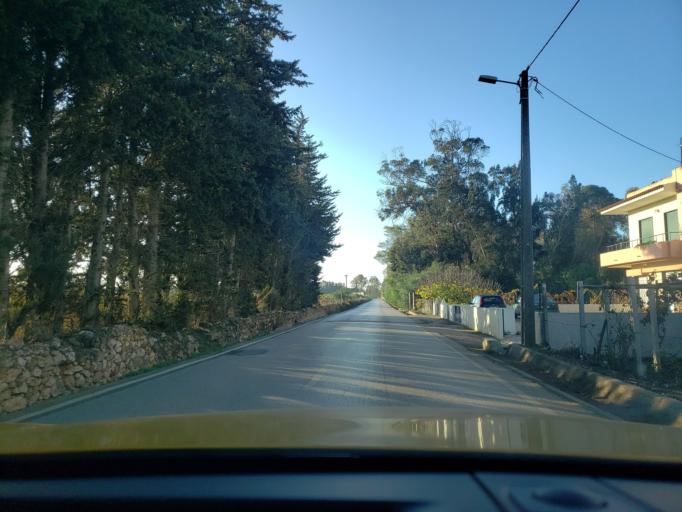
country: PT
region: Faro
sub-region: Portimao
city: Alvor
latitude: 37.1663
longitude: -8.5777
